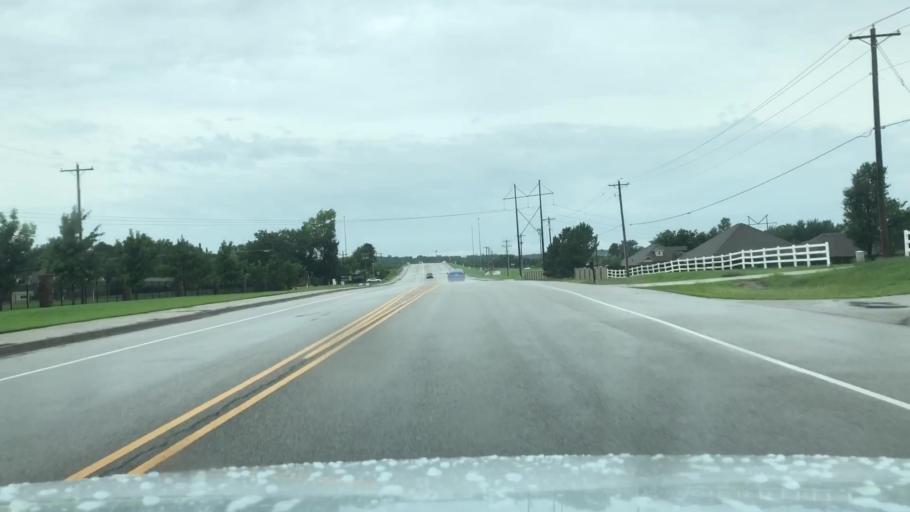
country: US
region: Oklahoma
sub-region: Tulsa County
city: Jenks
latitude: 36.0029
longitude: -96.0050
